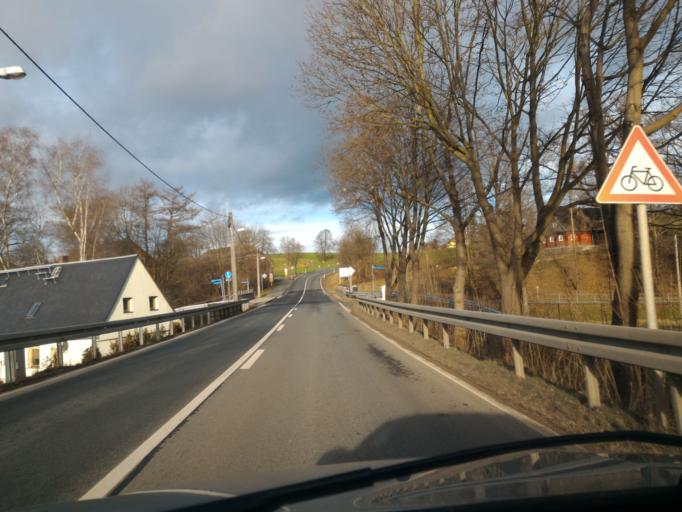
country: DE
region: Saxony
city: Neusalza-Spremberg
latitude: 51.0421
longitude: 14.5169
